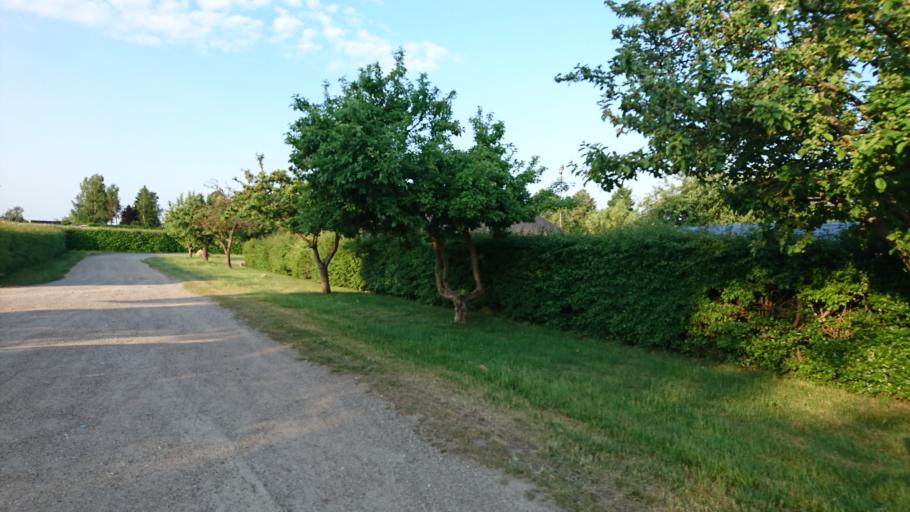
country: DK
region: Capital Region
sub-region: Egedal Kommune
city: Smorumnedre
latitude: 55.7203
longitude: 12.3289
